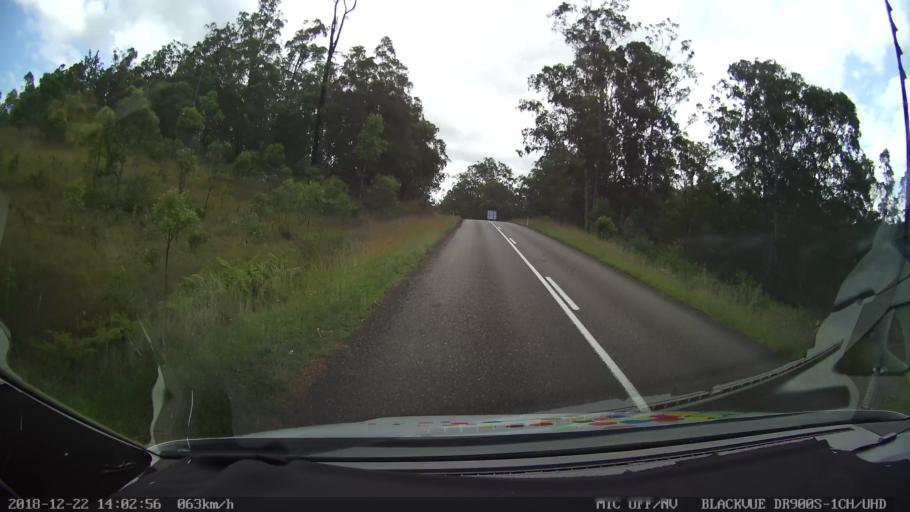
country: AU
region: New South Wales
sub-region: Clarence Valley
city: Coutts Crossing
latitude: -29.9267
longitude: 152.7442
